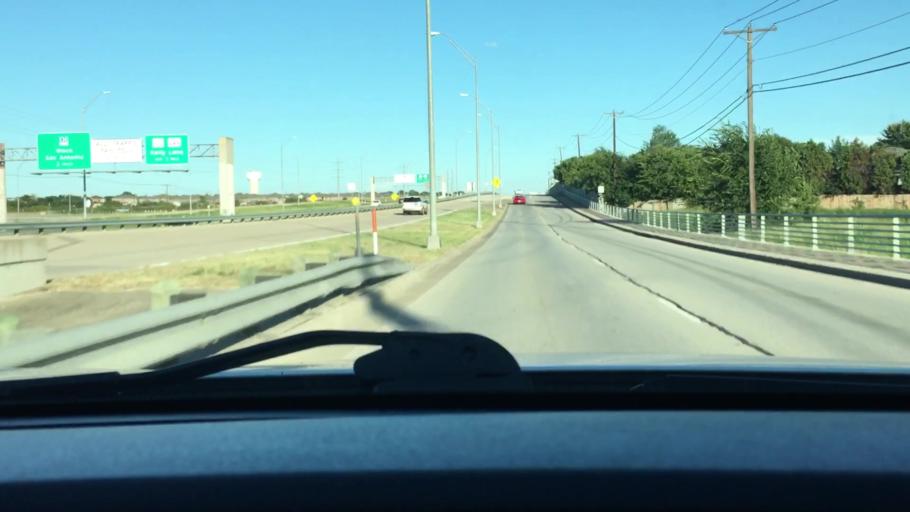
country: US
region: Texas
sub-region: Travis County
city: Windemere
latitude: 30.4882
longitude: -97.6344
